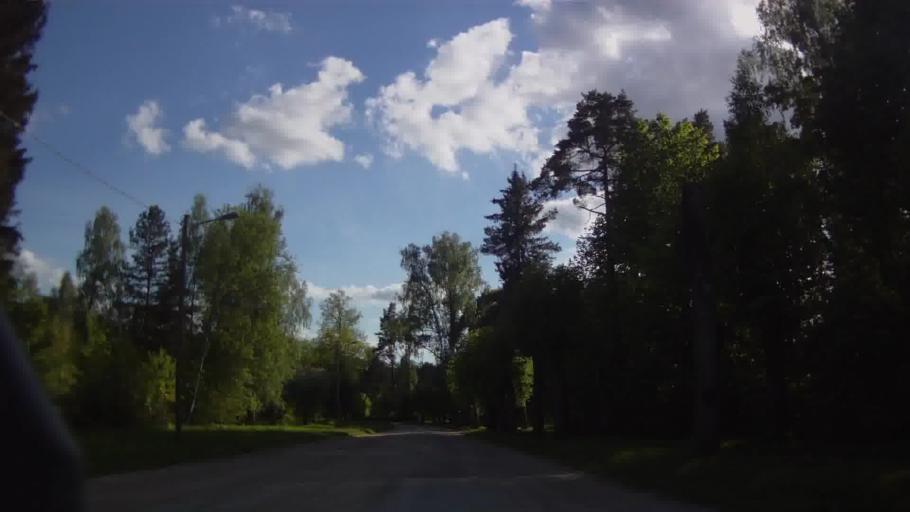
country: LV
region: Baldone
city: Baldone
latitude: 56.7449
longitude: 24.4074
